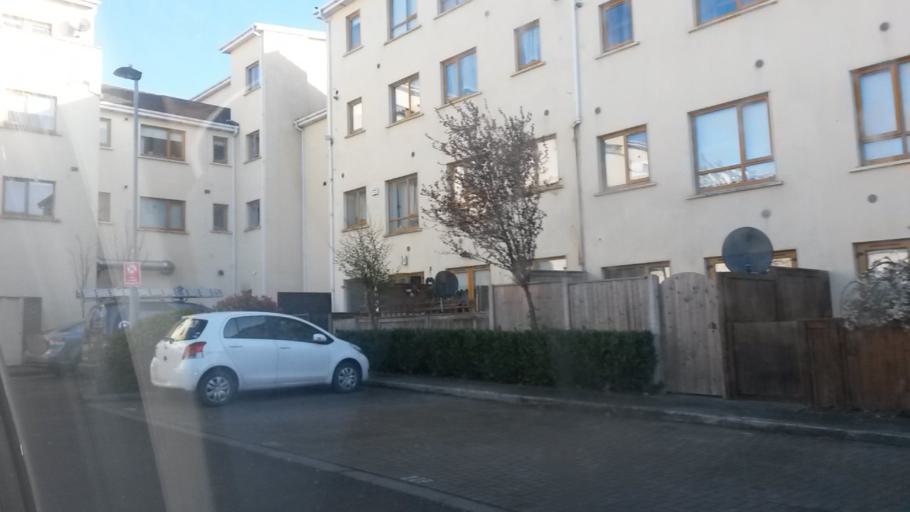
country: IE
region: Leinster
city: Ballymun
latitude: 53.4042
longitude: -6.2838
